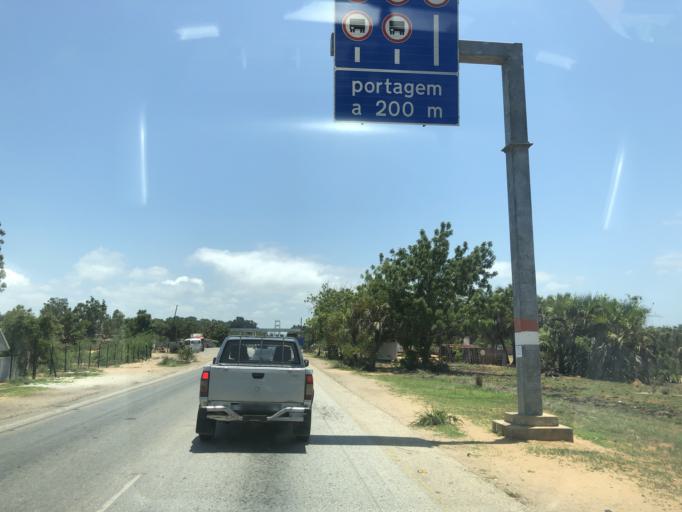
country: AO
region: Luanda
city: Luanda
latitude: -9.3175
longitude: 13.1547
